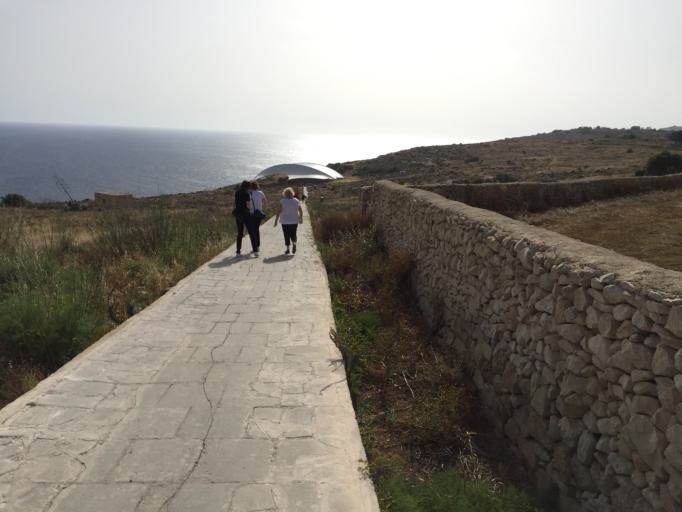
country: MT
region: Il-Qrendi
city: Qrendi
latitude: 35.8271
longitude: 14.4406
